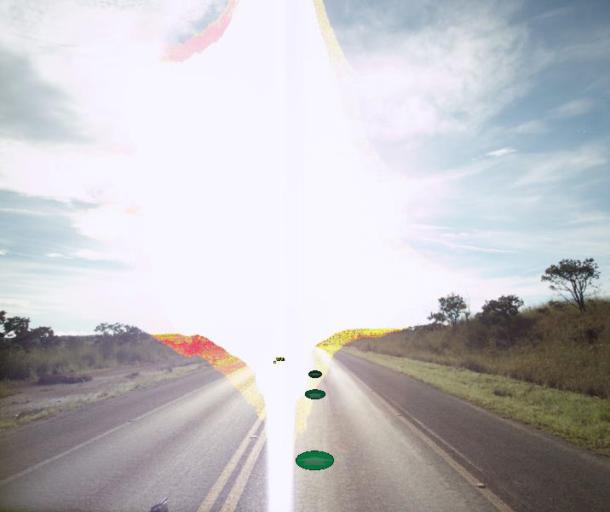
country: BR
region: Goias
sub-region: Pirenopolis
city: Pirenopolis
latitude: -15.7753
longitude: -48.5157
